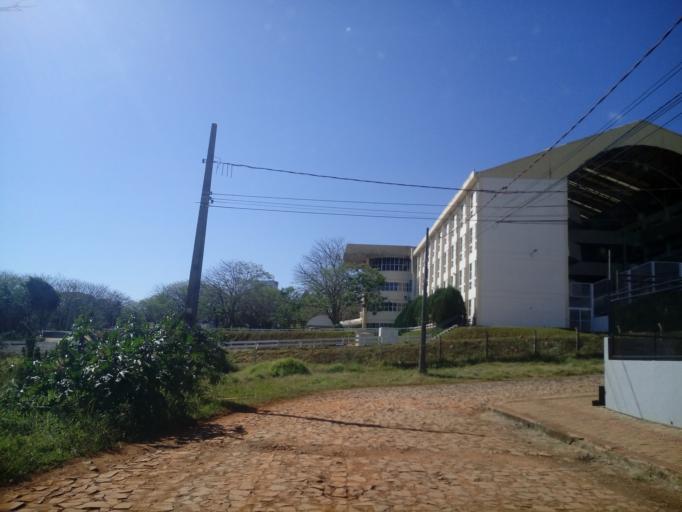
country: BR
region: Santa Catarina
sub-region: Chapeco
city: Chapeco
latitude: -27.0927
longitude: -52.6691
